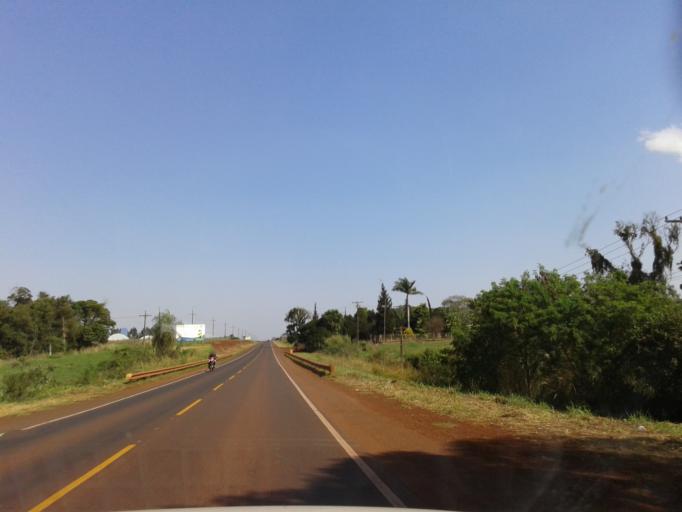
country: PY
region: Alto Parana
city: Santa Rita
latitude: -25.7225
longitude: -55.0361
